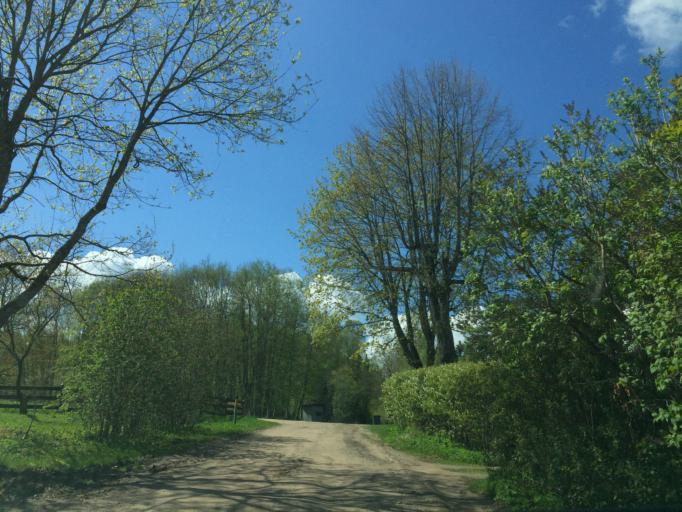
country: LV
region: Baldone
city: Baldone
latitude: 56.7414
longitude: 24.3686
